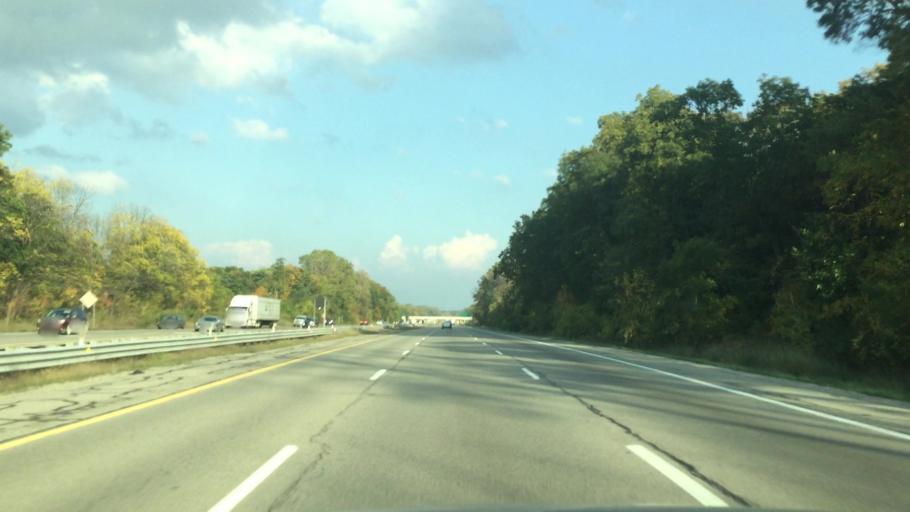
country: US
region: Michigan
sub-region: Washtenaw County
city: Dexter
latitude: 42.2977
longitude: -83.8894
